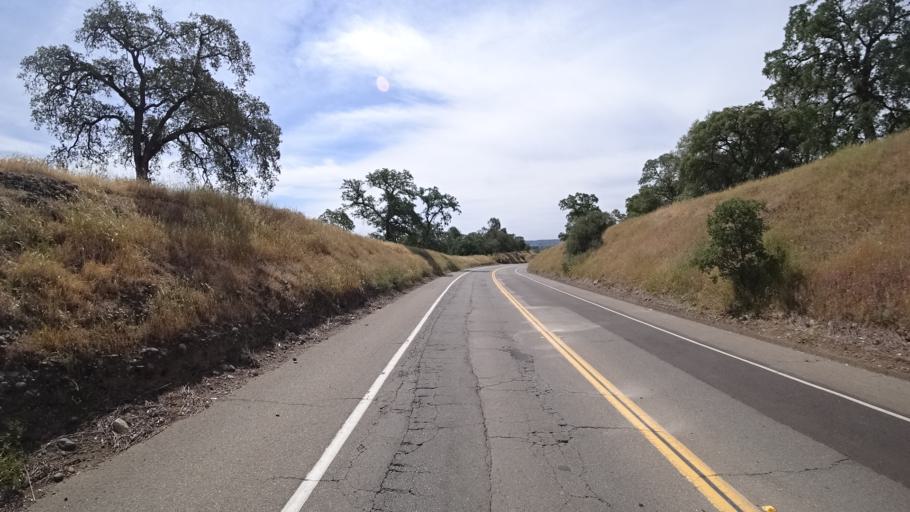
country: US
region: California
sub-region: Placer County
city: Loomis
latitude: 38.8447
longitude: -121.2207
